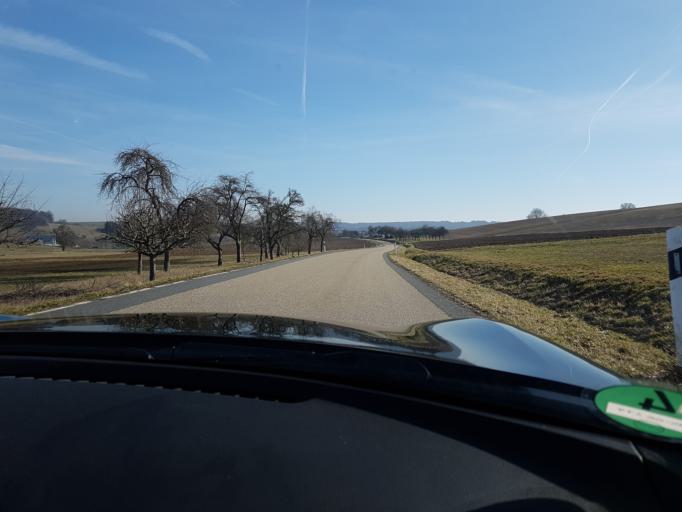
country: DE
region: Baden-Wuerttemberg
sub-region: Karlsruhe Region
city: Rosenberg
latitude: 49.4050
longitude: 9.5389
